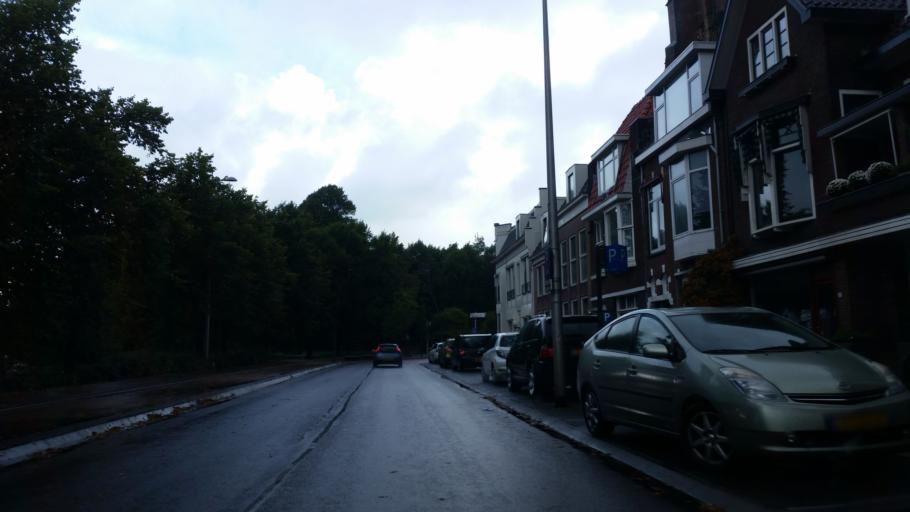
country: NL
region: Friesland
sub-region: Gemeente Leeuwarden
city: Bilgaard
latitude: 53.2025
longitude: 5.7891
